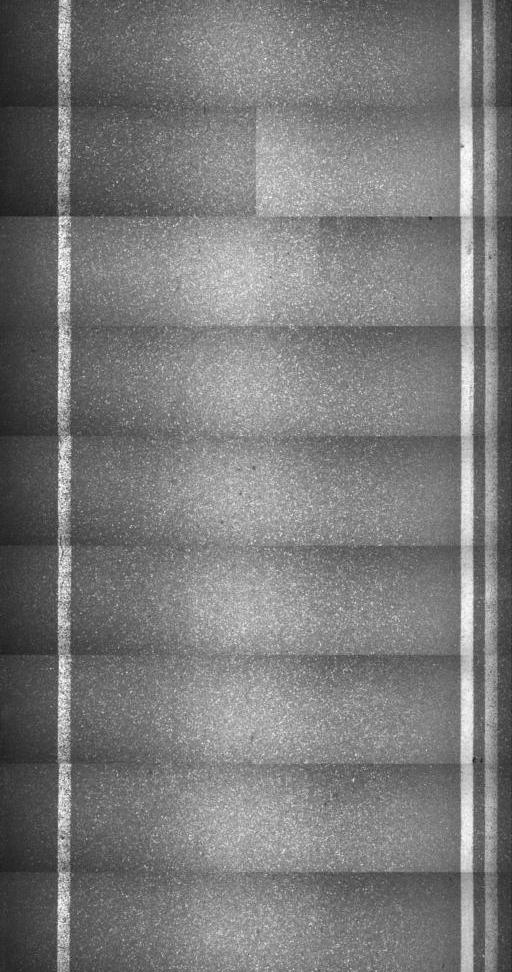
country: US
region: Vermont
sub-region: Washington County
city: Northfield
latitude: 44.2035
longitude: -72.6369
